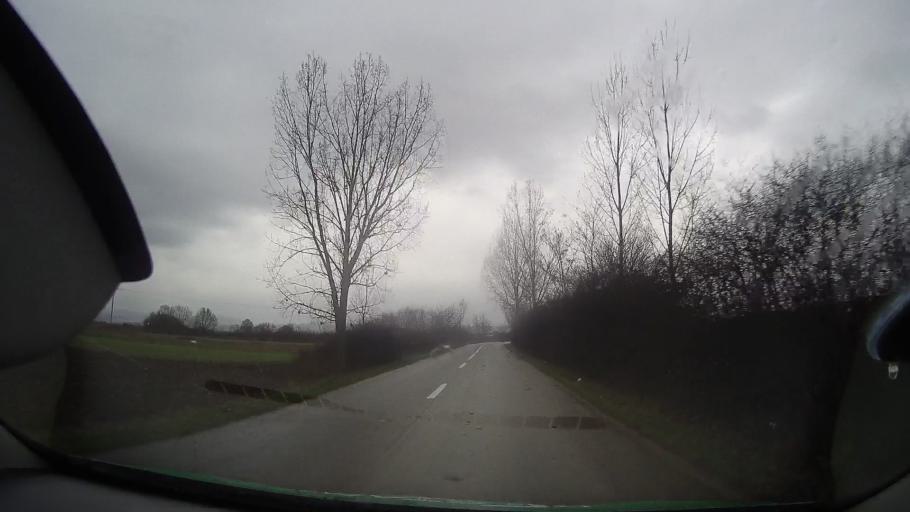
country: RO
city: Capalna
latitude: 46.7218
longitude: 22.0860
